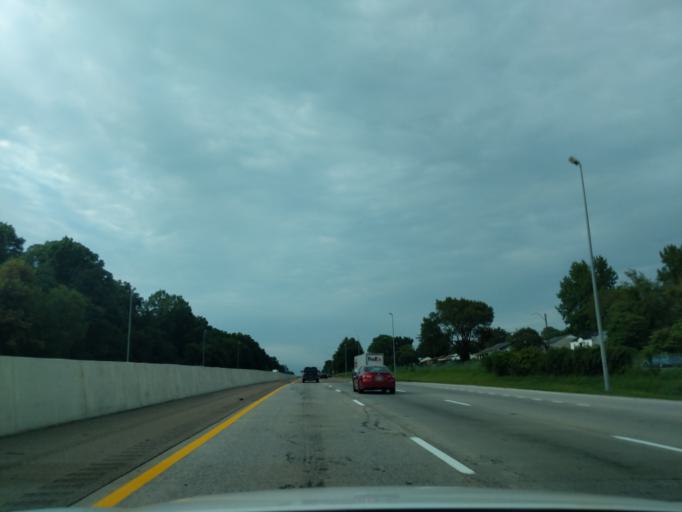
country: US
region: Tennessee
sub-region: Shelby County
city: New South Memphis
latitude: 35.0901
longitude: -90.0766
